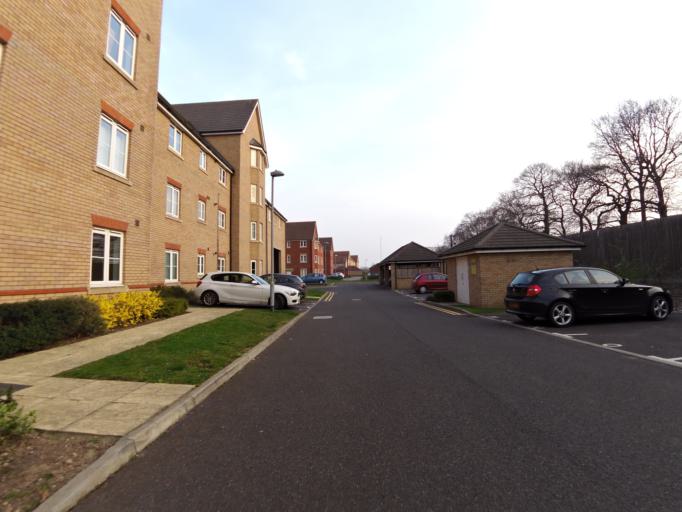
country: GB
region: England
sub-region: Suffolk
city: Ipswich
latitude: 52.0451
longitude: 1.1519
